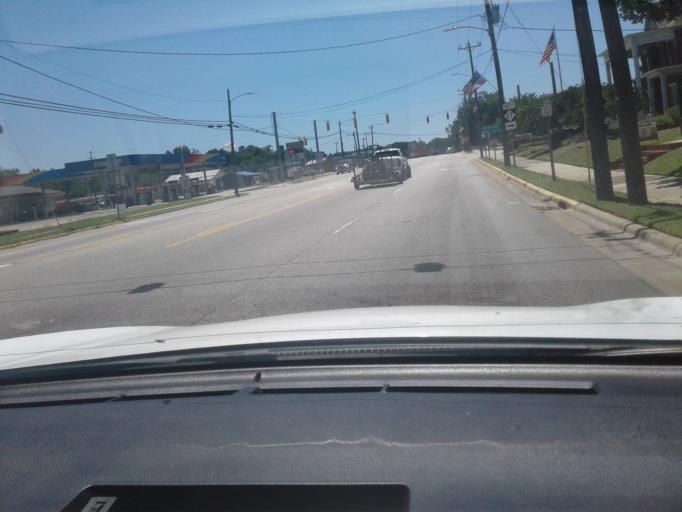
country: US
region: North Carolina
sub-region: Harnett County
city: Lillington
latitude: 35.3936
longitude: -78.8184
